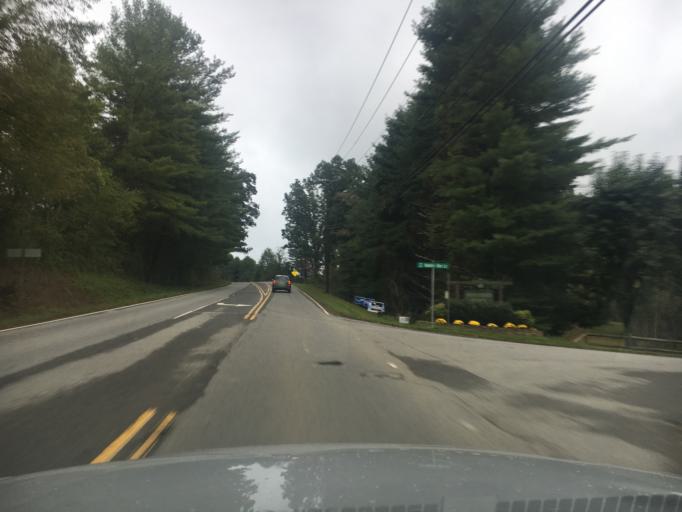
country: US
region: North Carolina
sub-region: Henderson County
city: Horse Shoe
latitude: 35.3417
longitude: -82.5470
